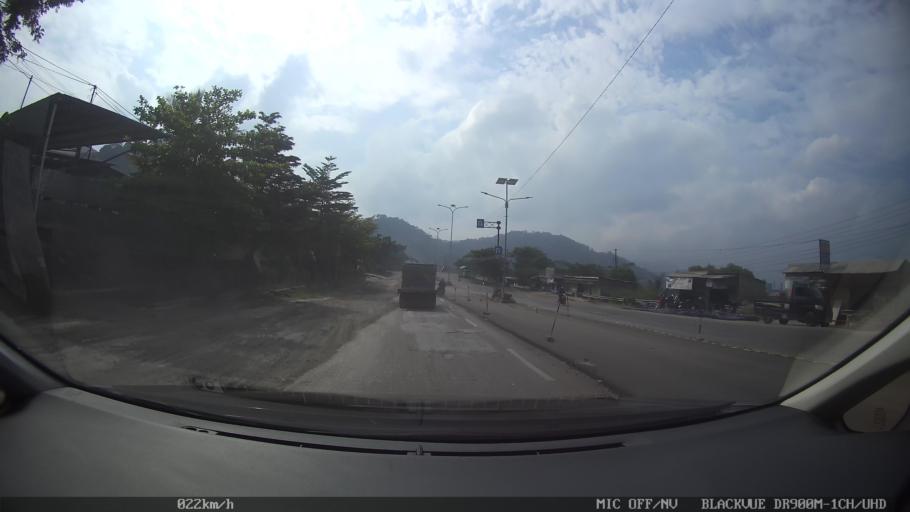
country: ID
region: Lampung
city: Panjang
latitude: -5.4413
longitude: 105.3077
